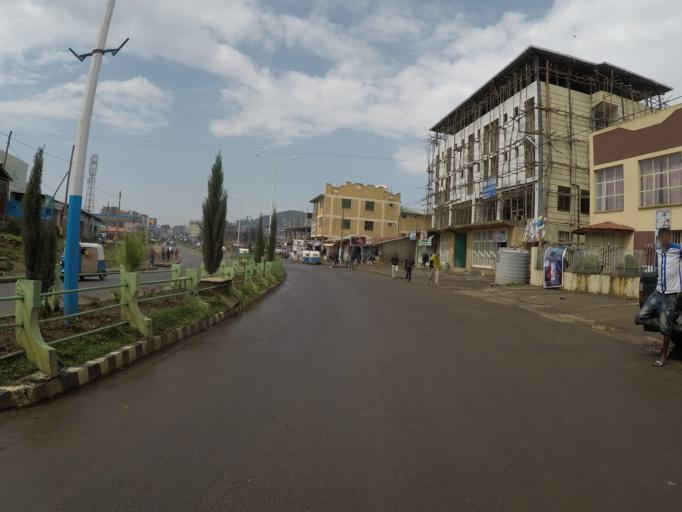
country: ET
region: Amhara
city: Debark'
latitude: 13.1528
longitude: 37.8984
